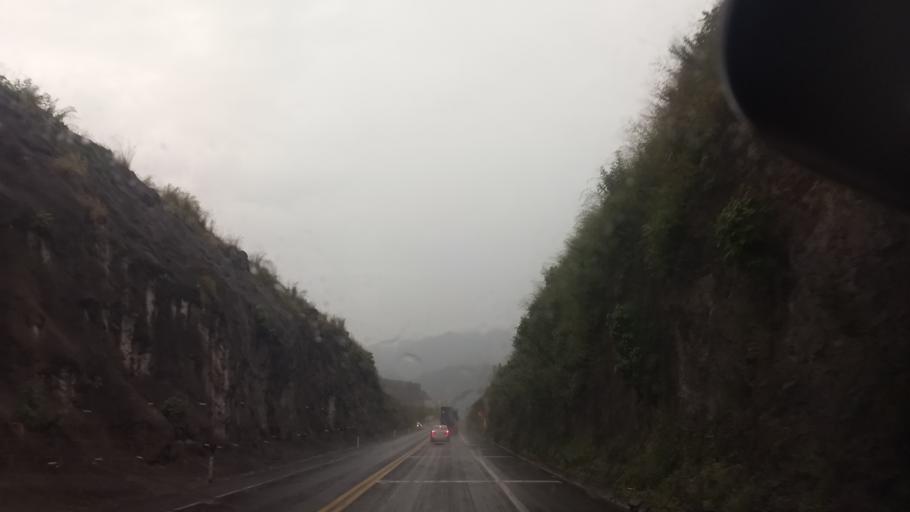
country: MX
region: Jalisco
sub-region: Tonila
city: San Marcos
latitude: 19.4385
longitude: -103.4781
